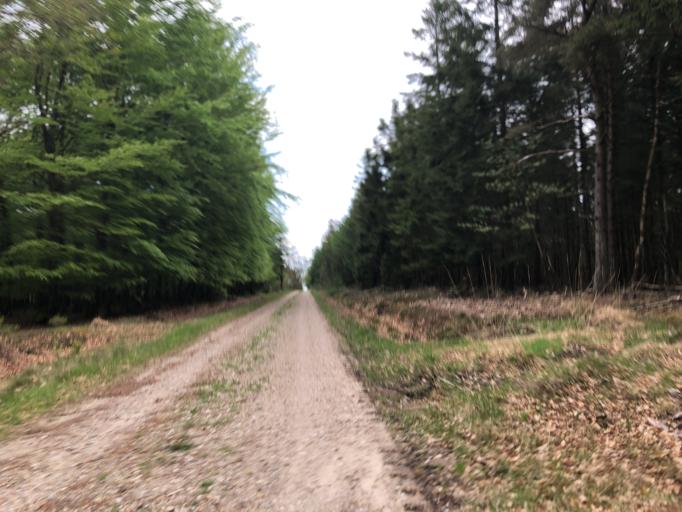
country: DK
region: Central Jutland
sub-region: Holstebro Kommune
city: Ulfborg
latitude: 56.2906
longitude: 8.4294
